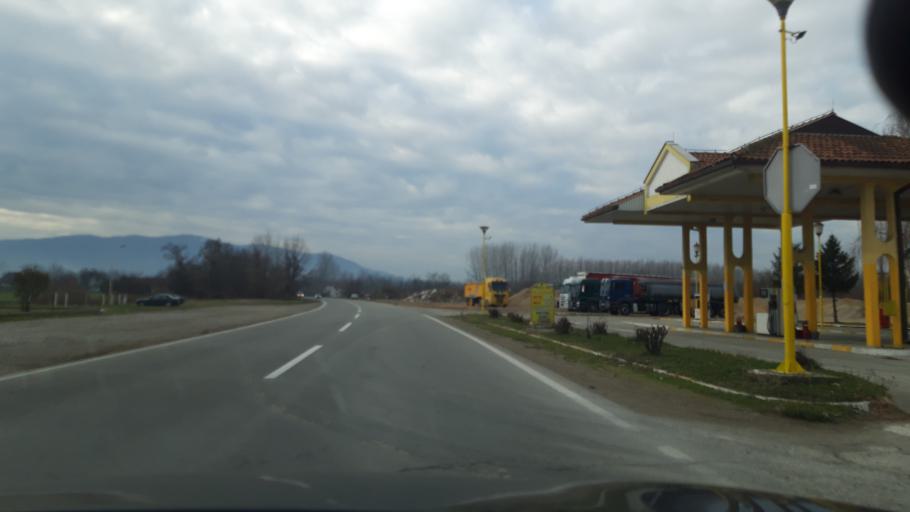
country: RS
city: Lipnicki Sor
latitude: 44.5641
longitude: 19.2012
